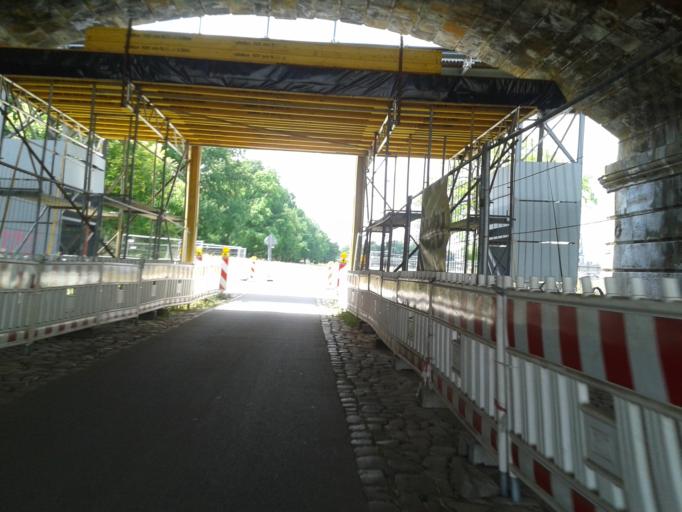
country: DE
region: Saxony
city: Dresden
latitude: 51.0563
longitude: 13.7556
